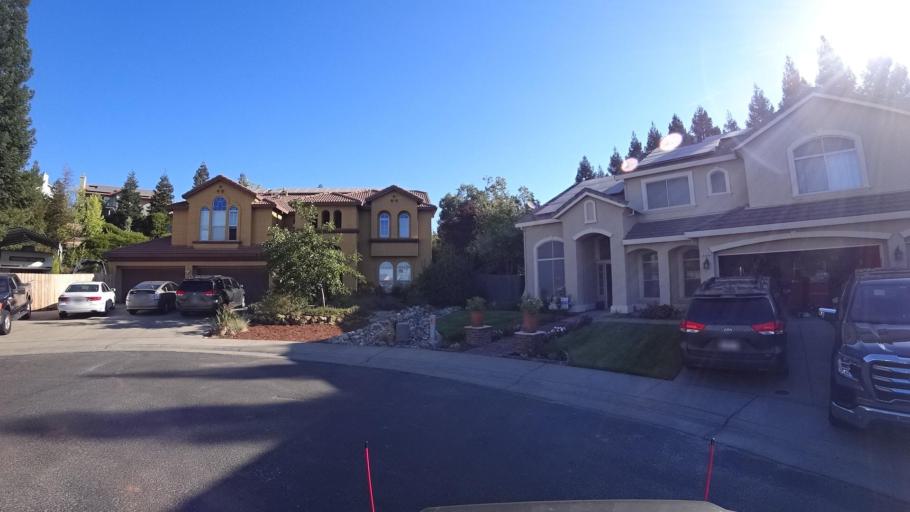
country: US
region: California
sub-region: Placer County
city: Rocklin
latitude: 38.8234
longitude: -121.2781
